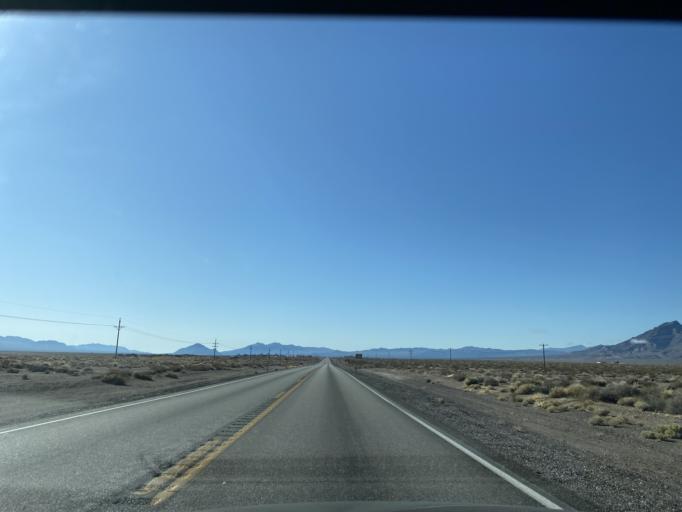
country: US
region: Nevada
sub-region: Nye County
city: Pahrump
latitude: 36.4377
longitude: -116.4220
